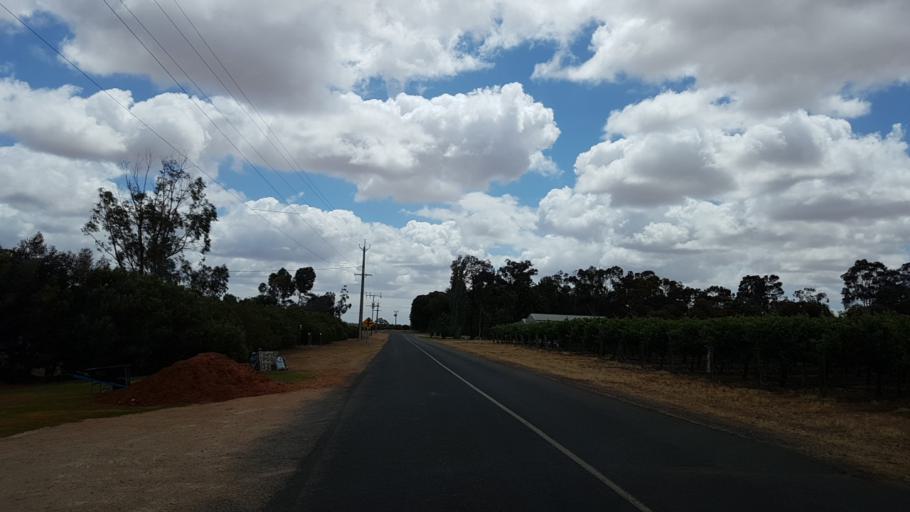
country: AU
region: South Australia
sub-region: Loxton Waikerie
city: Waikerie
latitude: -34.1723
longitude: 140.0312
